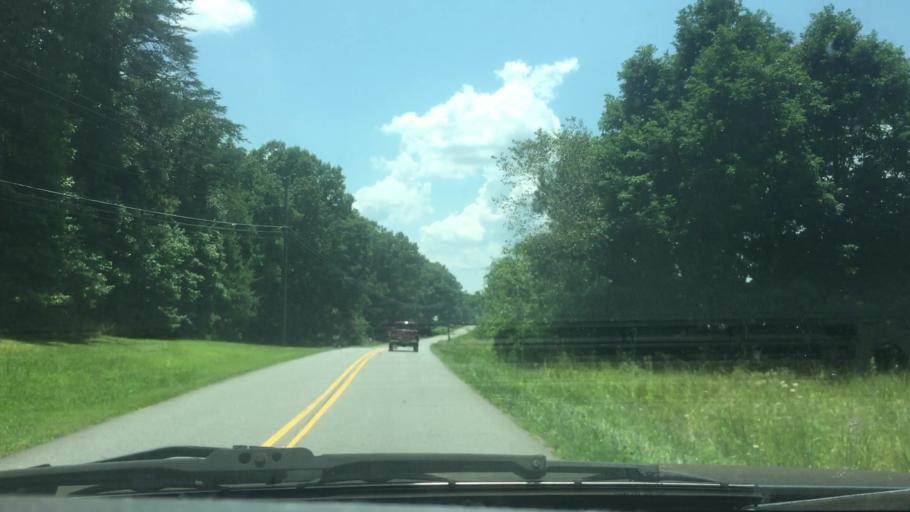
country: US
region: Georgia
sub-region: Bartow County
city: Rydal
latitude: 34.3244
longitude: -84.7091
